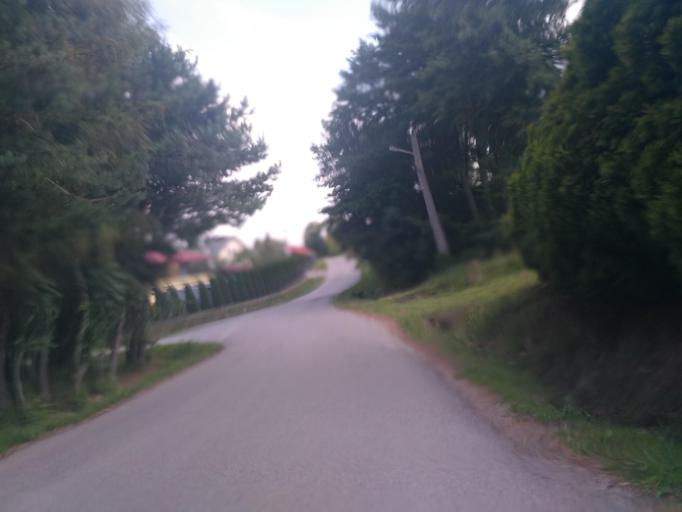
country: PL
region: Subcarpathian Voivodeship
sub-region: Powiat lancucki
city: Kraczkowa
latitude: 50.0353
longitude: 22.1691
